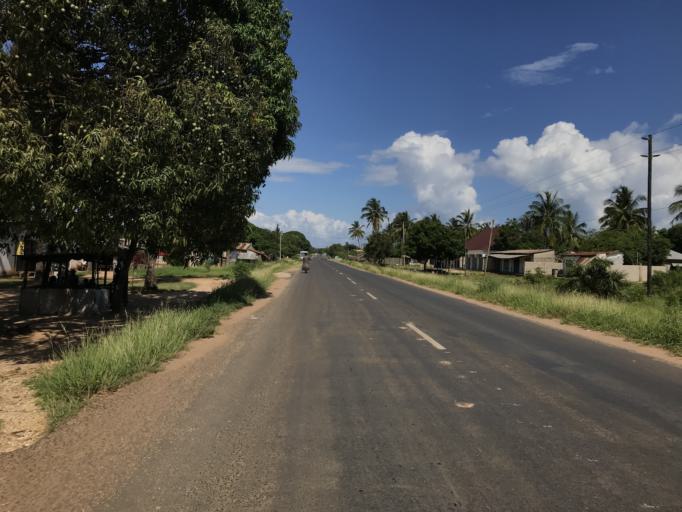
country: TZ
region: Dar es Salaam
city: Dar es Salaam
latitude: -6.8755
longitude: 39.4109
